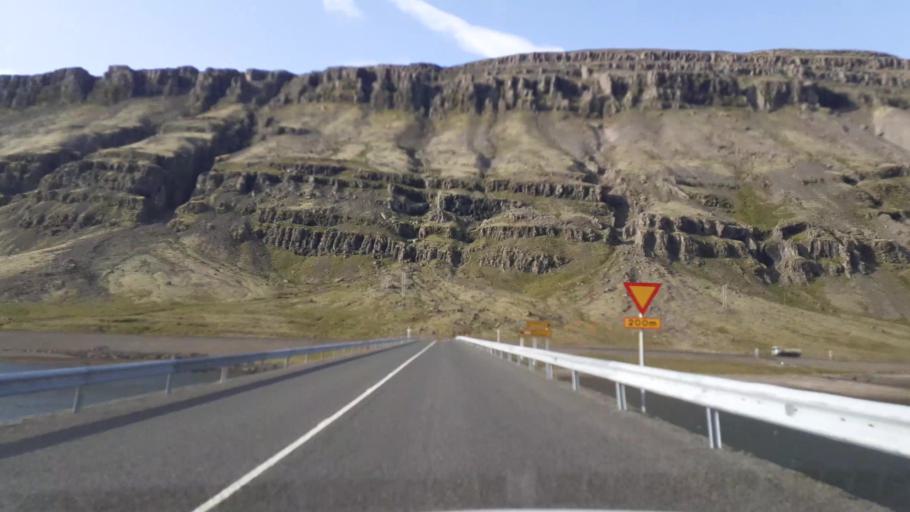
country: IS
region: East
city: Reydarfjoerdur
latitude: 64.7875
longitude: -14.4906
